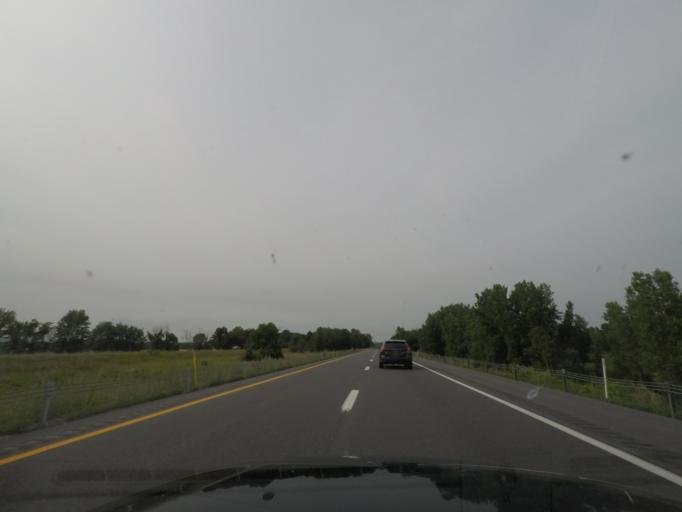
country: US
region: New York
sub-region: Clinton County
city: Cumberland Head
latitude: 44.7641
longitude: -73.4314
